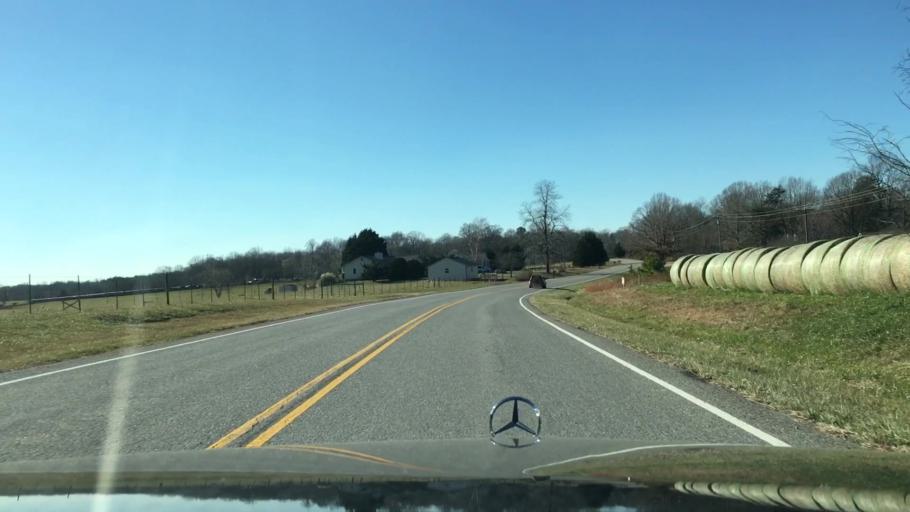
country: US
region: Virginia
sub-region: City of Bedford
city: Bedford
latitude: 37.2209
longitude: -79.4870
